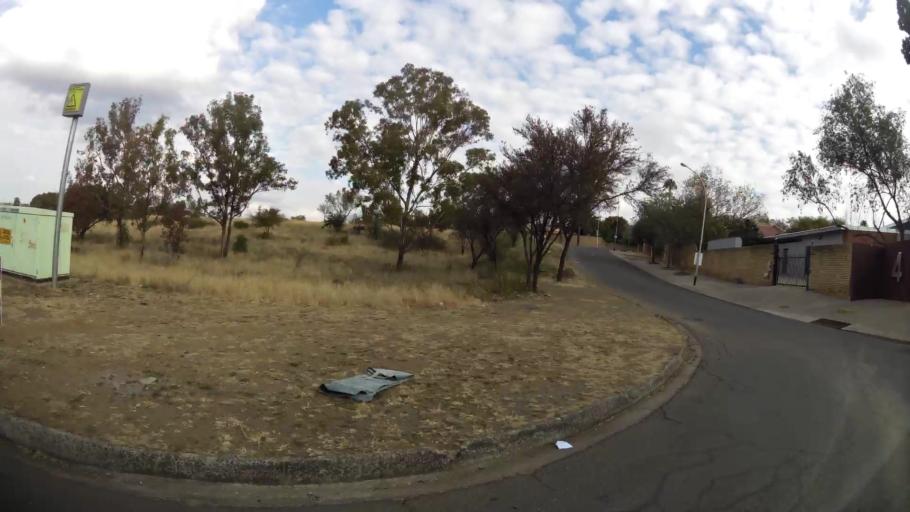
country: ZA
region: Orange Free State
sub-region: Mangaung Metropolitan Municipality
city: Bloemfontein
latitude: -29.0813
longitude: 26.2029
